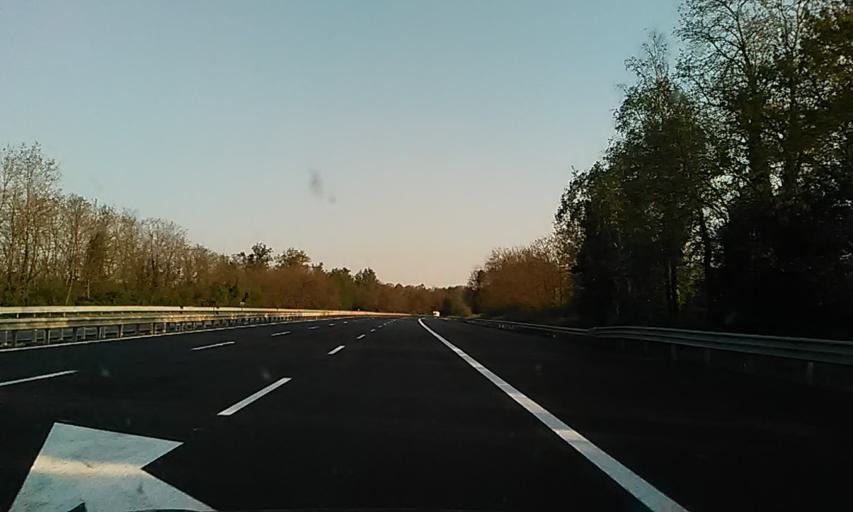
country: IT
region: Piedmont
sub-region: Provincia di Novara
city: Veruno
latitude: 45.6894
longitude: 8.5421
